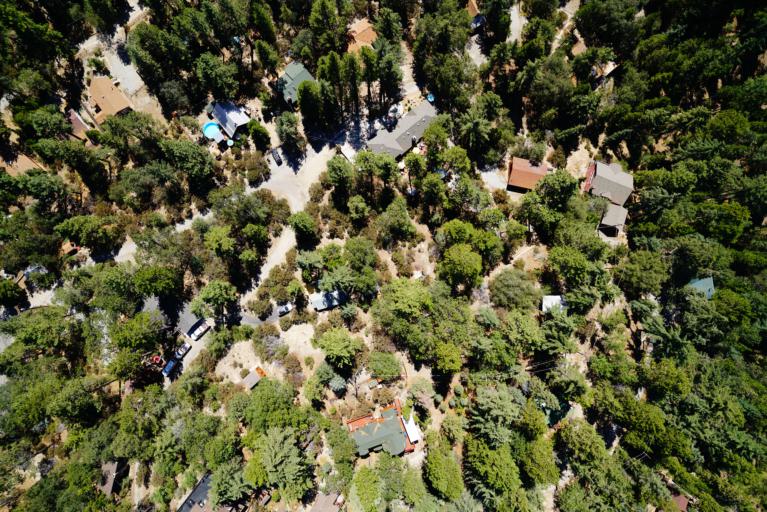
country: US
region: California
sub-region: Riverside County
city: Idyllwild-Pine Cove
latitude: 33.7603
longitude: -116.7406
